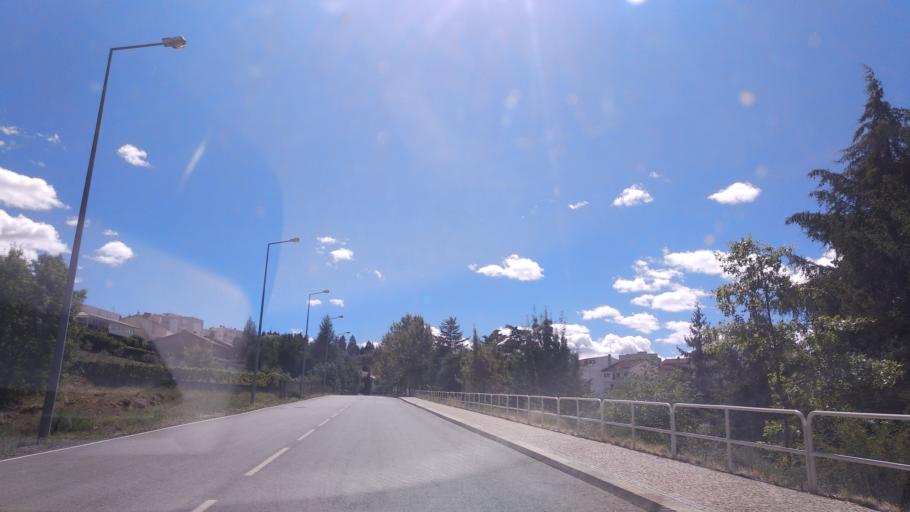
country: PT
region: Braganca
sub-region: Braganca Municipality
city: Braganca
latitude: 41.7965
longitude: -6.7606
